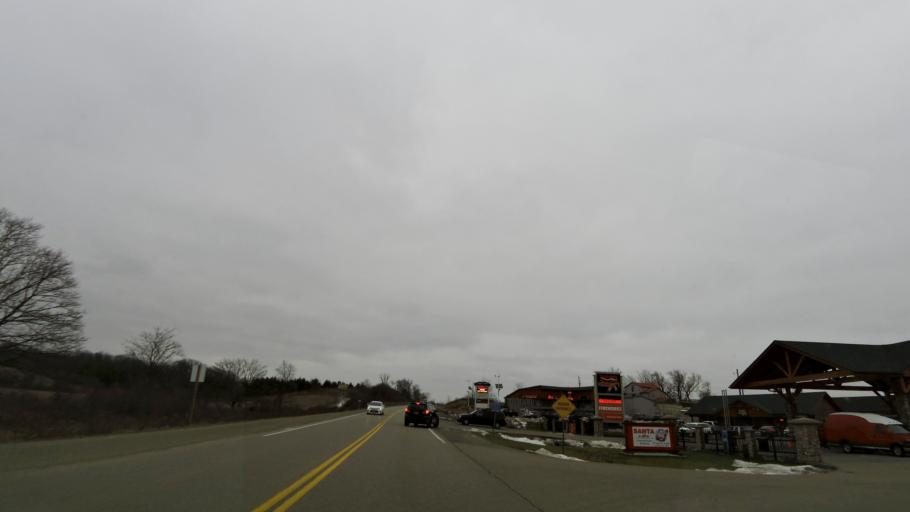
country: CA
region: Ontario
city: Brantford
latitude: 43.1169
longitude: -80.1131
